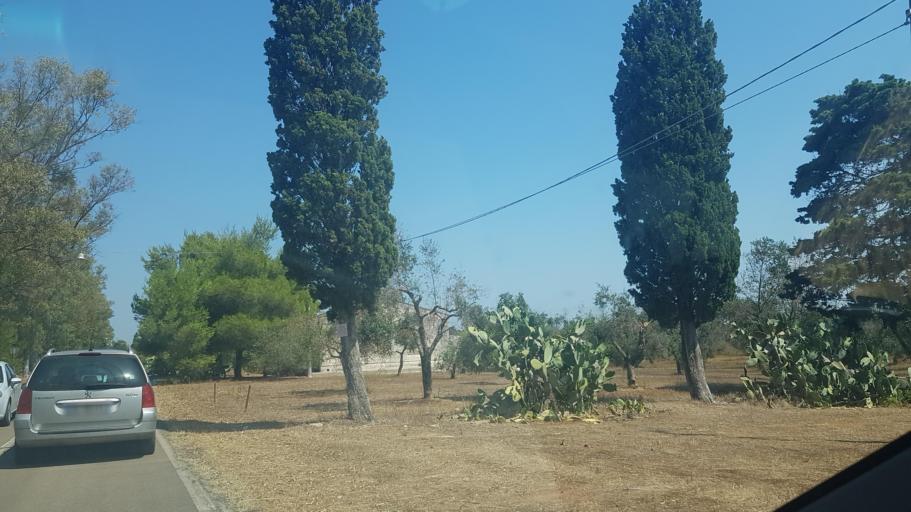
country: IT
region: Apulia
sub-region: Provincia di Lecce
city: Otranto
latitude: 40.1961
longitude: 18.4358
